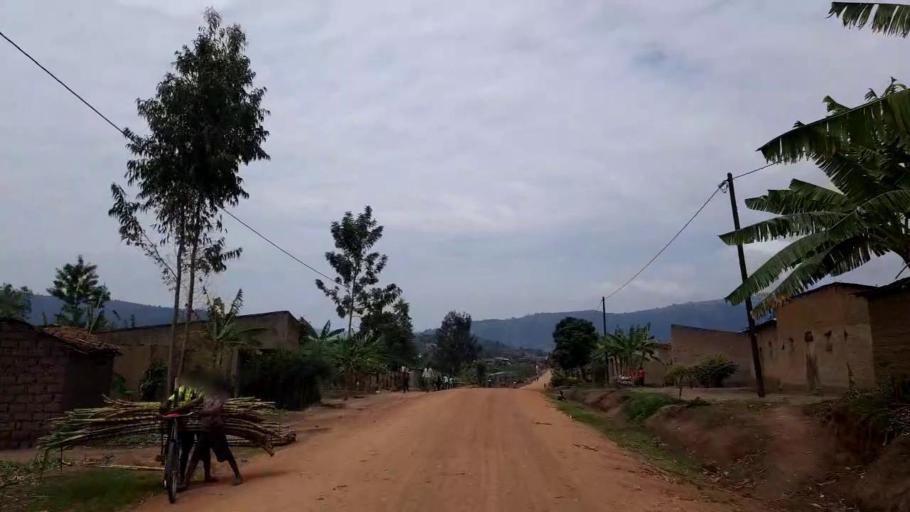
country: RW
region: Northern Province
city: Byumba
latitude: -1.4987
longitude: 30.2192
